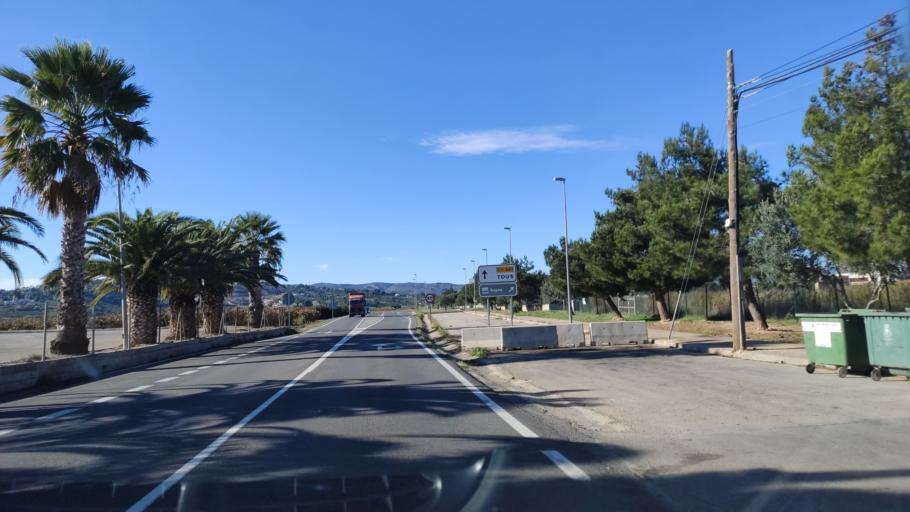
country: ES
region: Valencia
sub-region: Provincia de Valencia
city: Alberic
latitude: 39.1200
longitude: -0.5359
